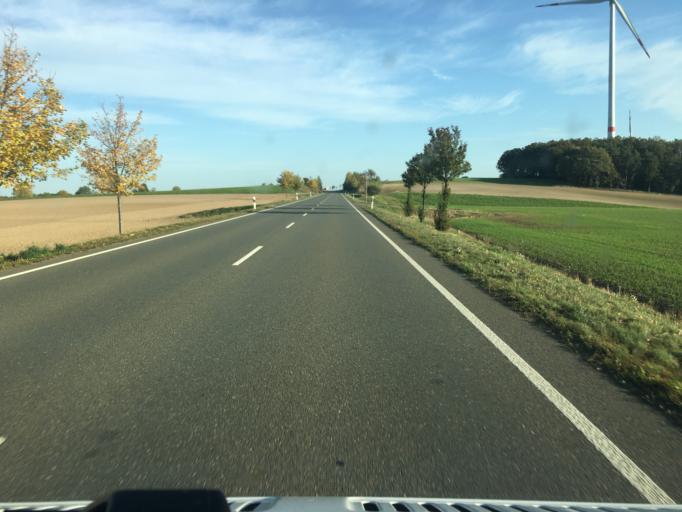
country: DE
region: Thuringia
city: Thonhausen
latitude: 50.8297
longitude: 12.3388
